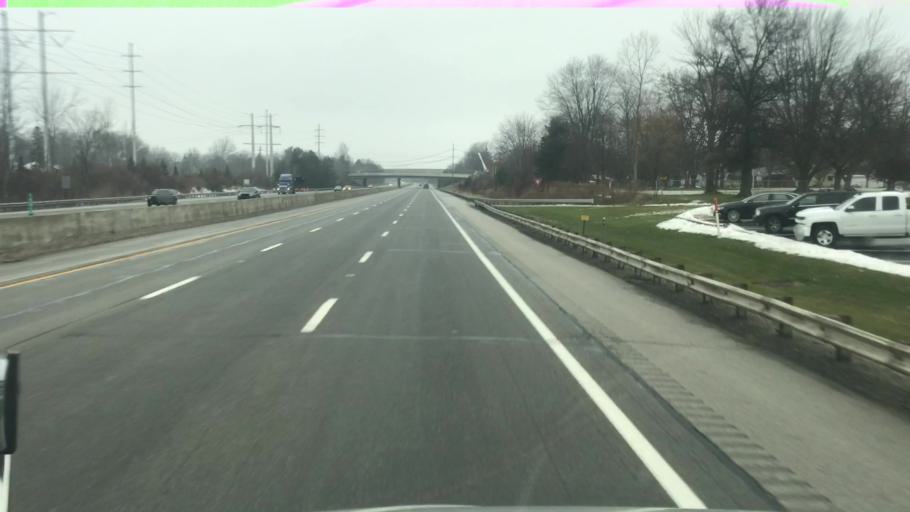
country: US
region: Ohio
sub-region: Cuyahoga County
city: Berea
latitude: 41.3488
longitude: -81.8616
